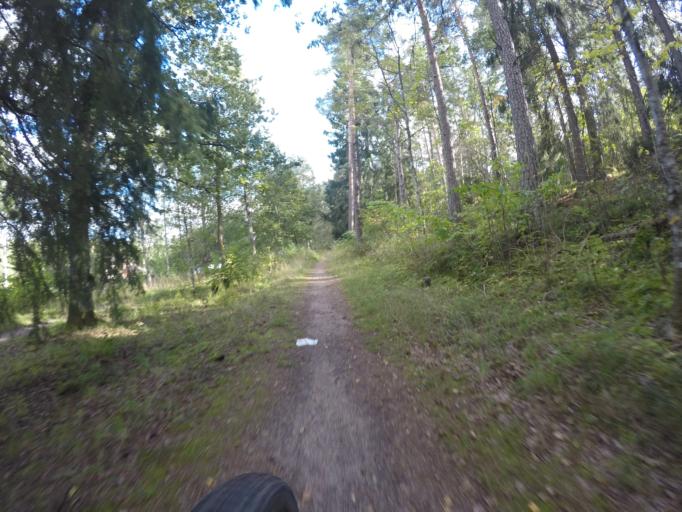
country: SE
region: Vaestmanland
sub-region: Kopings Kommun
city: Koping
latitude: 59.5120
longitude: 16.0107
